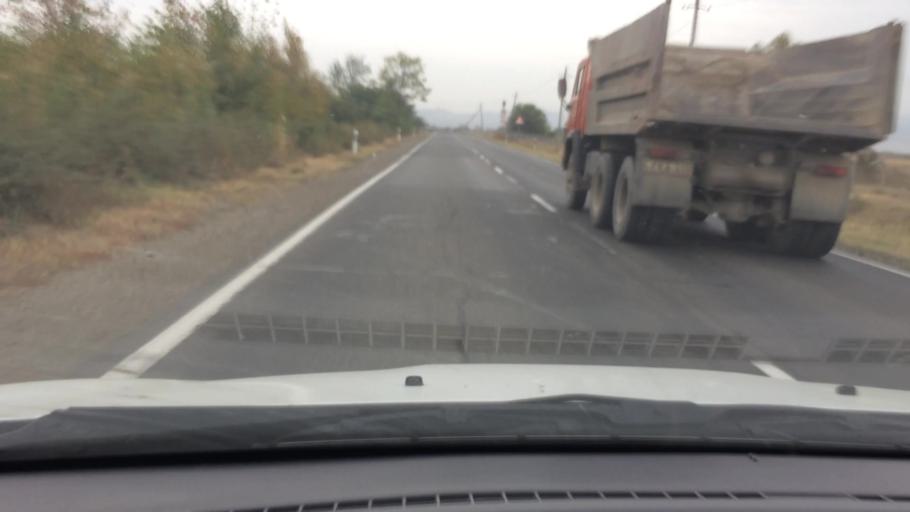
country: GE
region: Kvemo Kartli
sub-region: Marneuli
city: Marneuli
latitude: 41.4678
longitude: 44.8045
